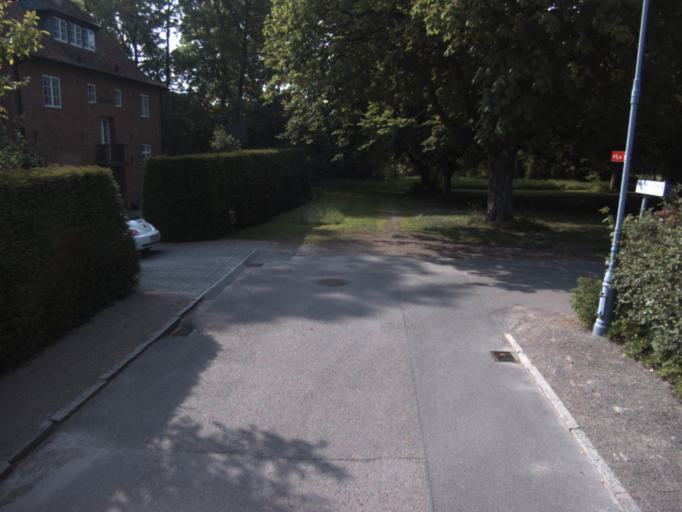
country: SE
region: Skane
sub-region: Helsingborg
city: Helsingborg
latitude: 56.0674
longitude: 12.6819
